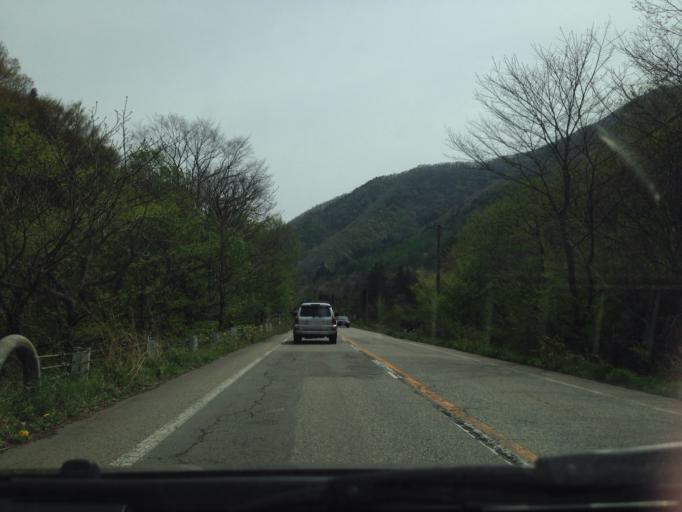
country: JP
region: Tochigi
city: Kuroiso
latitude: 37.0971
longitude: 139.7252
